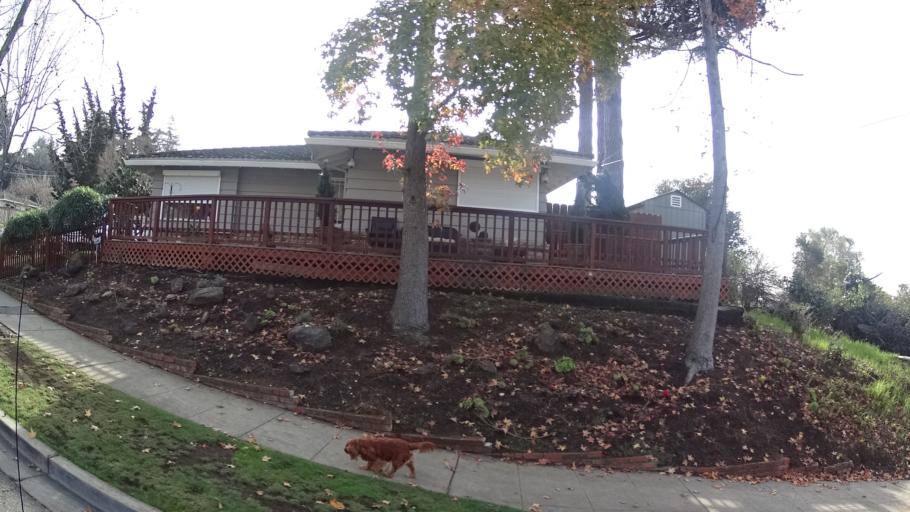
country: US
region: California
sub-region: Alameda County
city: Hayward
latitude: 37.6631
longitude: -122.0729
